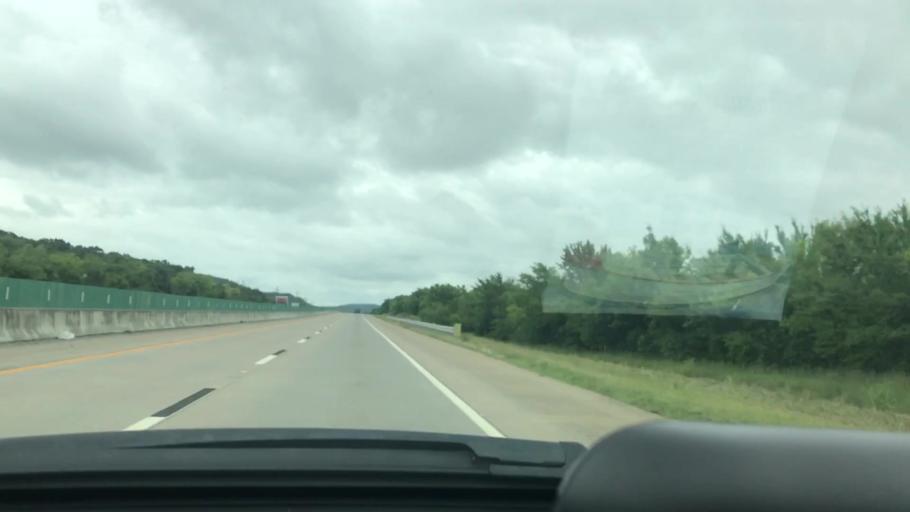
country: US
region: Oklahoma
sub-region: Pittsburg County
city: Krebs
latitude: 35.0712
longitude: -95.7046
